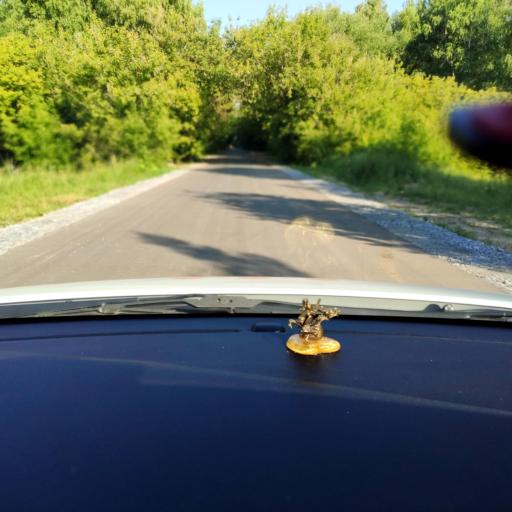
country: RU
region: Tatarstan
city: Stolbishchi
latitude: 55.6998
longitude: 49.2218
